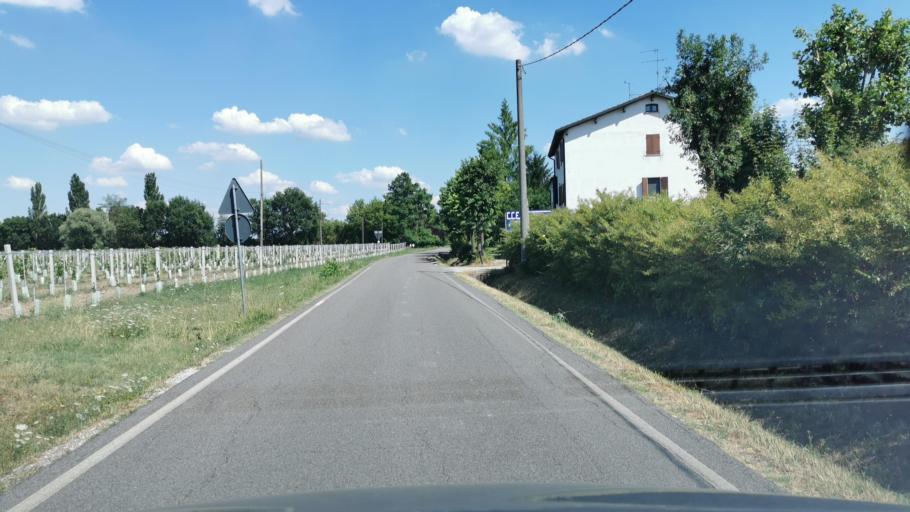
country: IT
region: Emilia-Romagna
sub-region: Provincia di Modena
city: Fossoli
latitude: 44.8150
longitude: 10.8947
